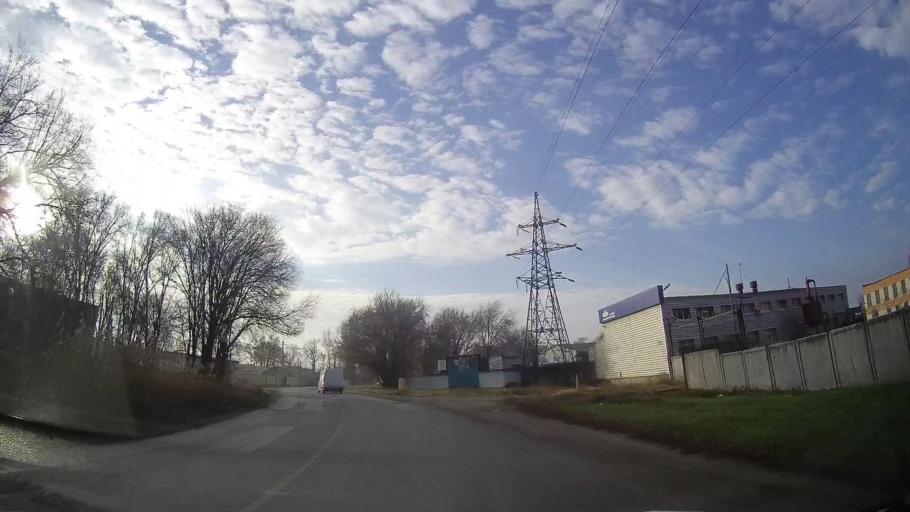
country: RU
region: Rostov
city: Bataysk
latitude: 47.1057
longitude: 39.7630
